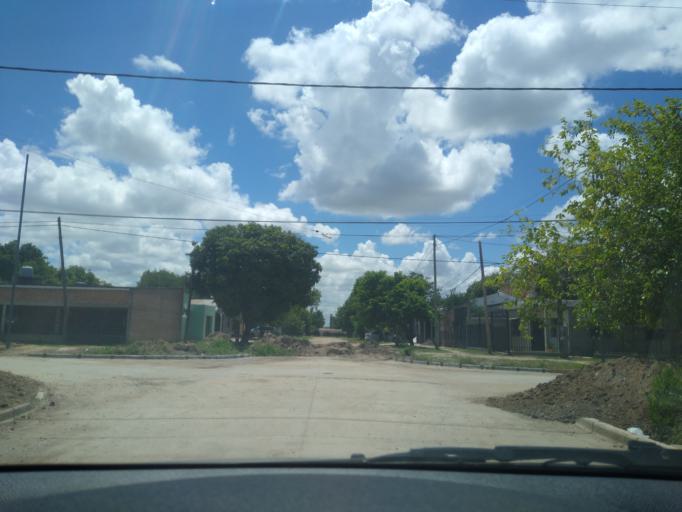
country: AR
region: Chaco
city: Barranqueras
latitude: -27.4782
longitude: -58.9326
